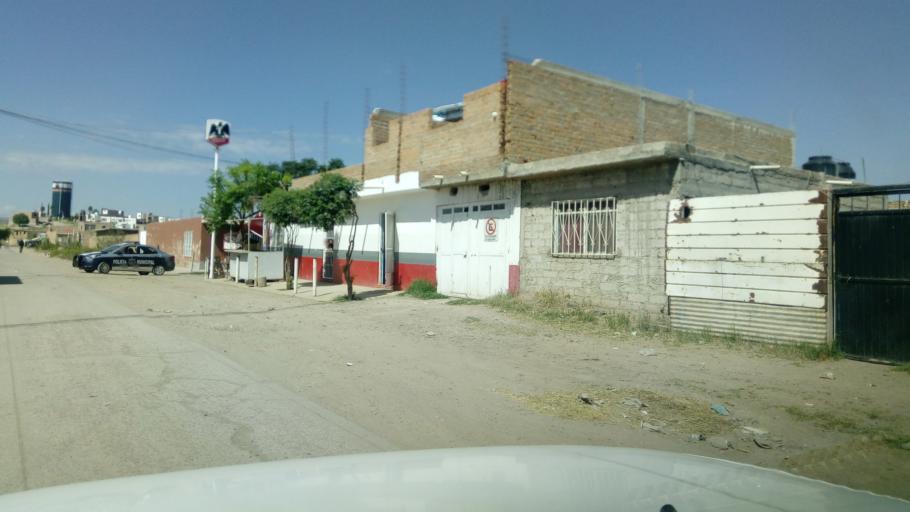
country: MX
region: Durango
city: Victoria de Durango
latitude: 23.9945
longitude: -104.6937
